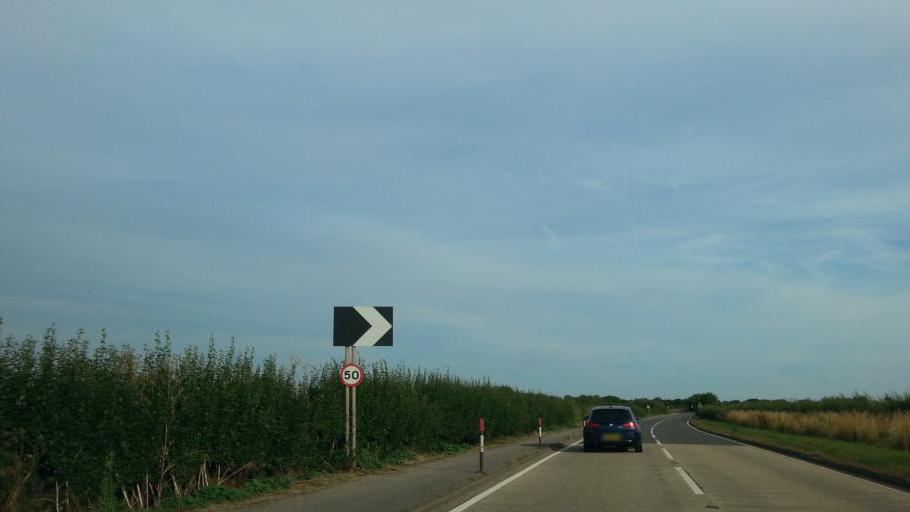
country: GB
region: England
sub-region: Nottinghamshire
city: Newark on Trent
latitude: 53.0867
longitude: -0.8352
